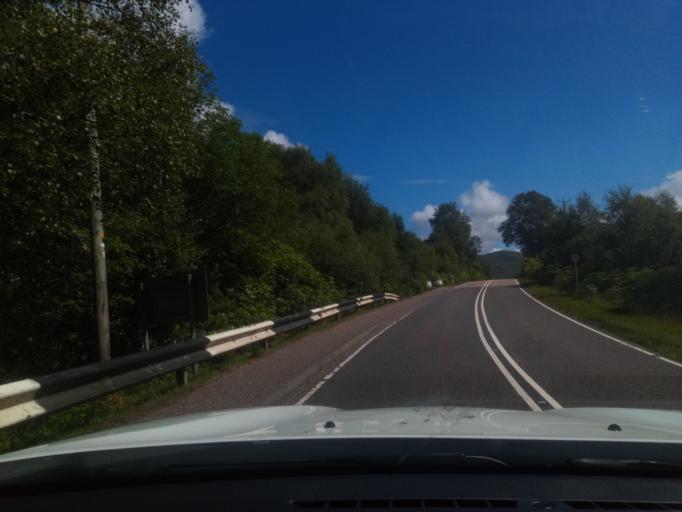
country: GB
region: Scotland
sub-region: Argyll and Bute
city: Isle Of Mull
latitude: 56.8823
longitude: -5.6620
